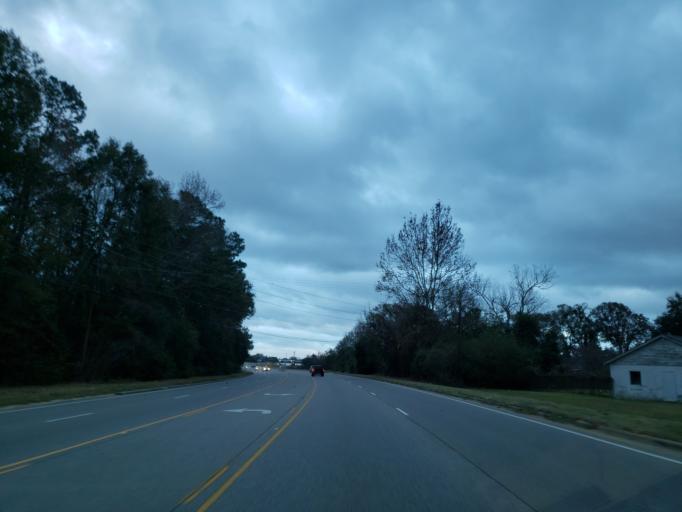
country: US
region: Alabama
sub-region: Mobile County
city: Prichard
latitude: 30.7801
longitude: -88.2686
